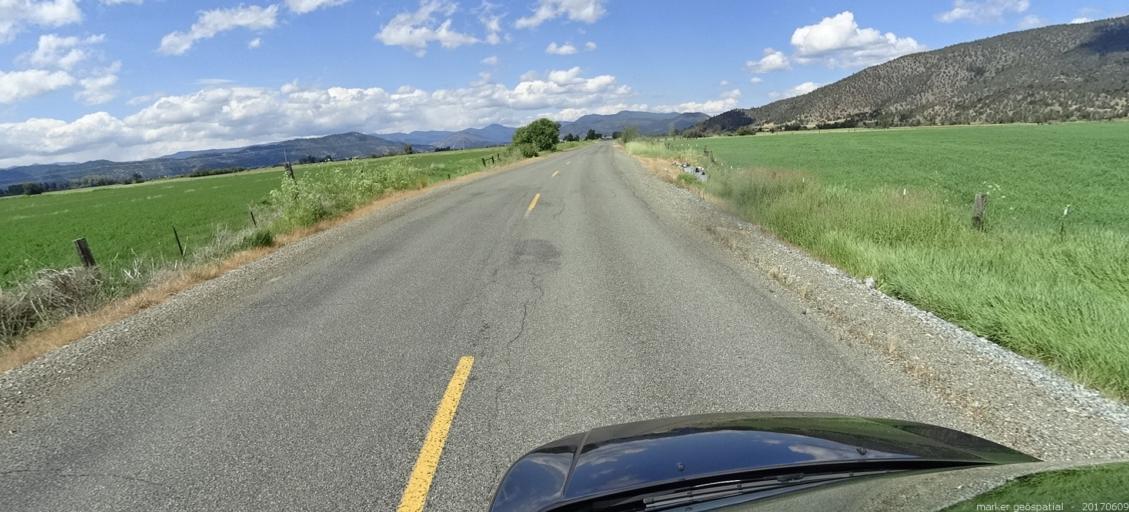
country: US
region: California
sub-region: Siskiyou County
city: Yreka
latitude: 41.5021
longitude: -122.8584
